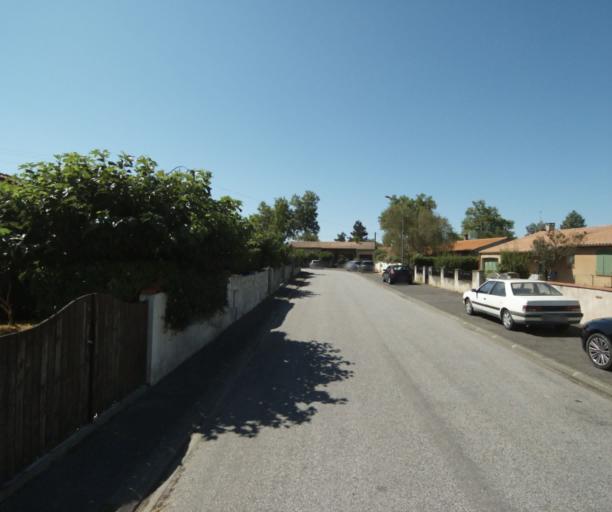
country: FR
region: Midi-Pyrenees
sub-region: Departement de la Haute-Garonne
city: Revel
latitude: 43.4652
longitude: 1.9905
